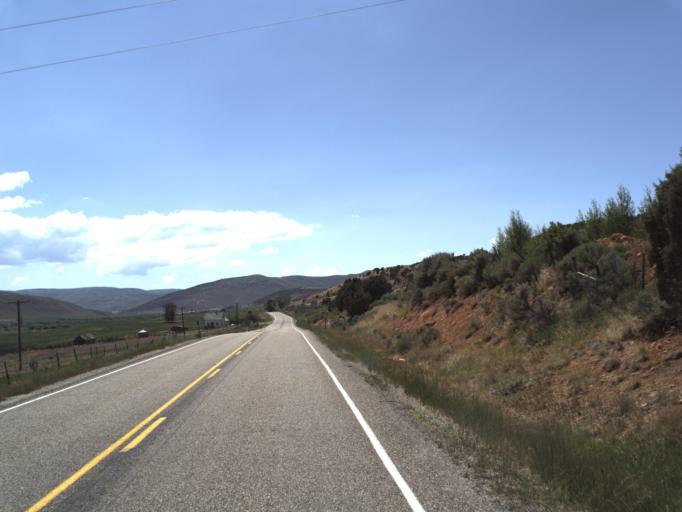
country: US
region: Utah
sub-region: Rich County
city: Randolph
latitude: 41.5159
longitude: -111.2119
